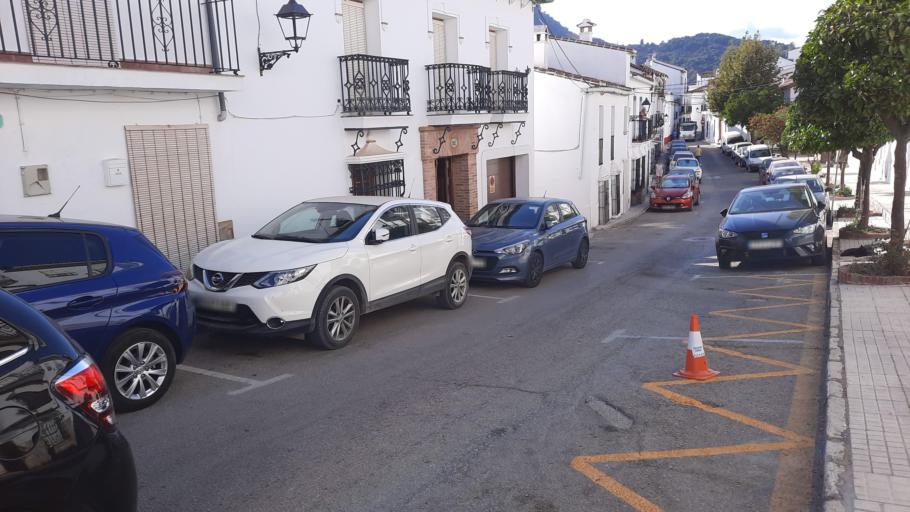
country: ES
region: Andalusia
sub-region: Provincia de Malaga
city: Gaucin
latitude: 36.5176
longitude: -5.3155
